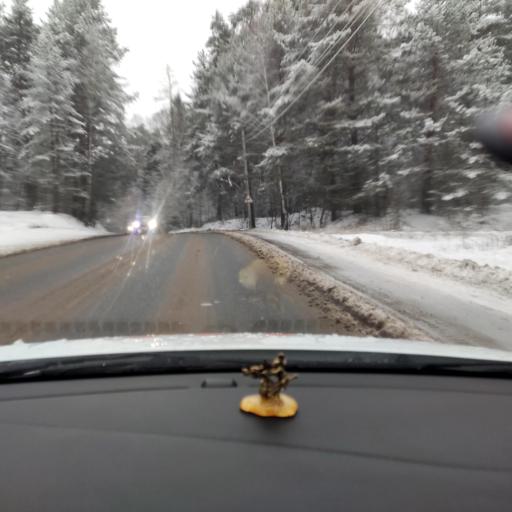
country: RU
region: Tatarstan
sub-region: Zelenodol'skiy Rayon
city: Zelenodolsk
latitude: 55.8636
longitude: 48.5354
